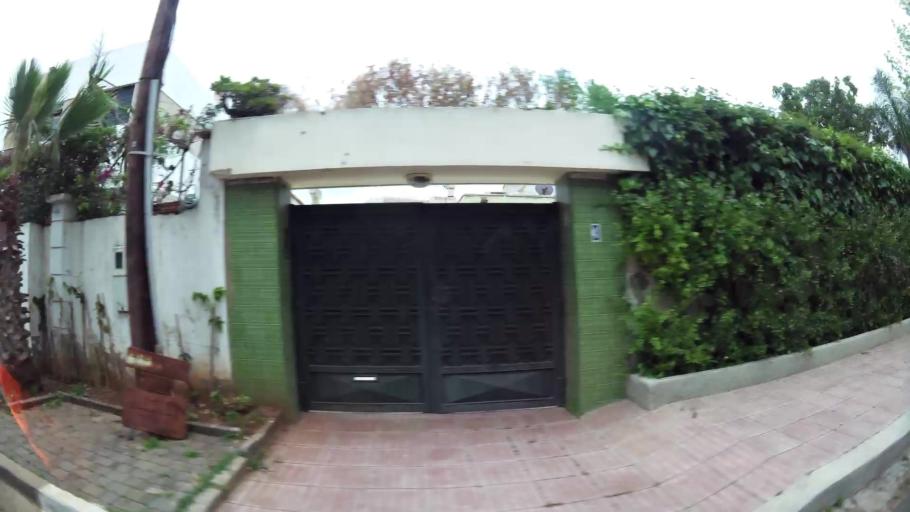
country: MA
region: Grand Casablanca
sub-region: Casablanca
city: Casablanca
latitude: 33.5546
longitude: -7.6207
